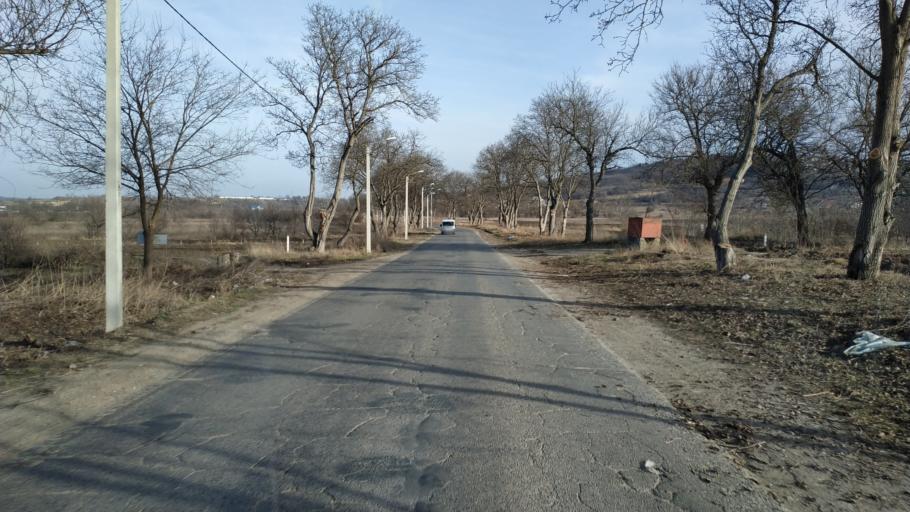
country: MD
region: Chisinau
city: Vatra
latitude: 47.0662
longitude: 28.7320
